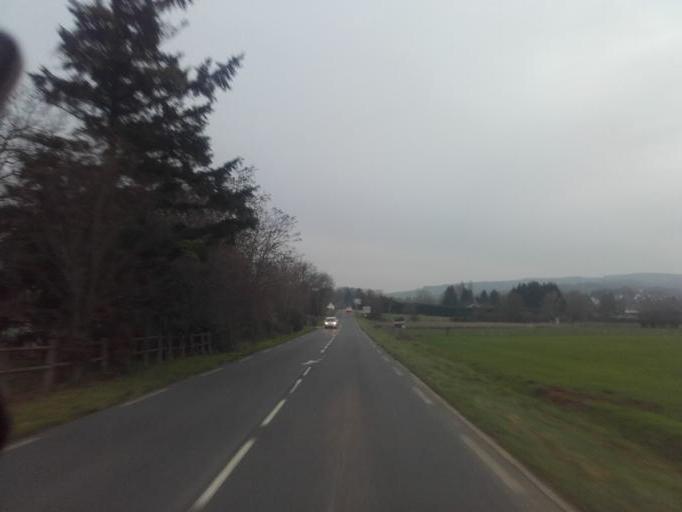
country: FR
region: Bourgogne
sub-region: Departement de Saone-et-Loire
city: Dracy-le-Fort
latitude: 46.8206
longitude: 4.7520
